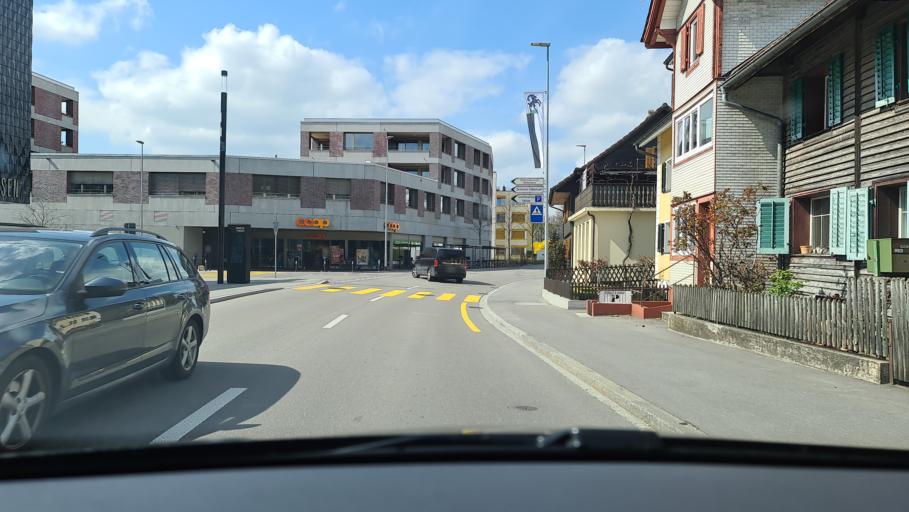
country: CH
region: Zug
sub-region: Zug
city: Steinhausen
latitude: 47.1967
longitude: 8.4837
